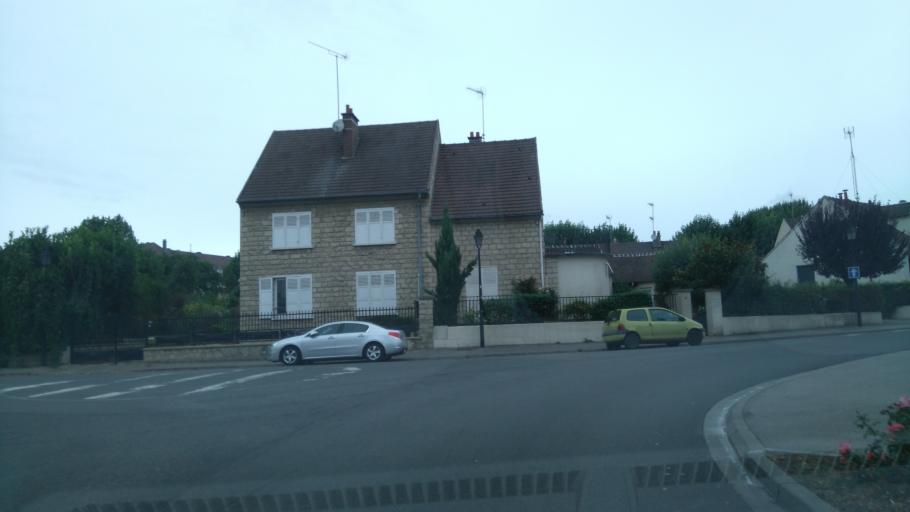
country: FR
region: Picardie
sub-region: Departement de l'Oise
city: Villers-sous-Saint-Leu
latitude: 49.2152
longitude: 2.4190
